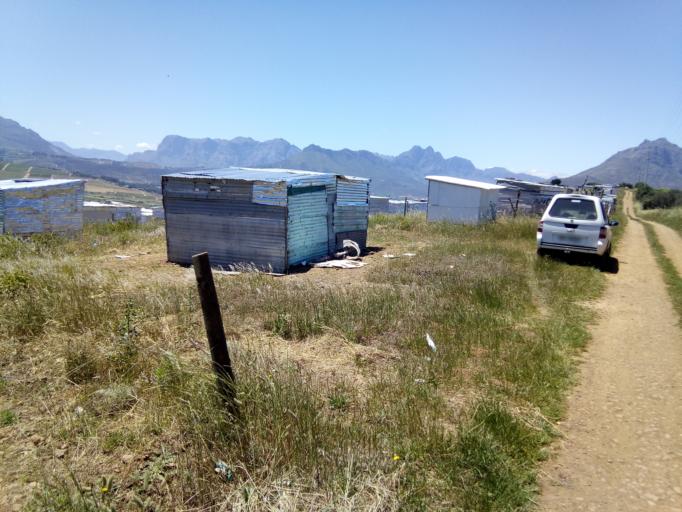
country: ZA
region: Western Cape
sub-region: Cape Winelands District Municipality
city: Stellenbosch
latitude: -33.9228
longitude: 18.8349
